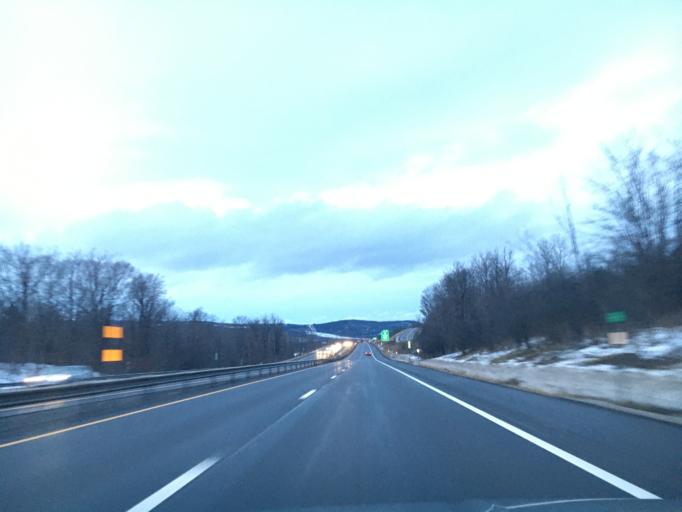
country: US
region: New York
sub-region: Onondaga County
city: Nedrow
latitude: 42.9377
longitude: -76.1322
